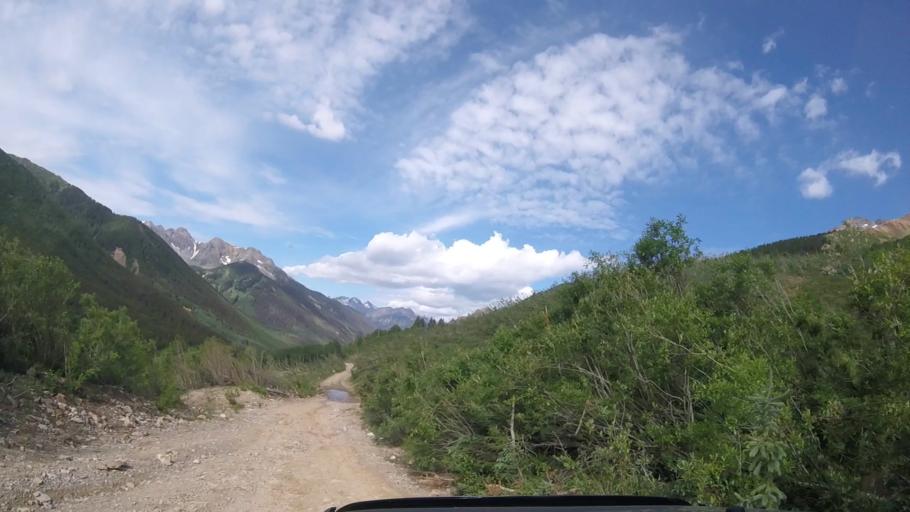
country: US
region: Colorado
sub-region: San Miguel County
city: Telluride
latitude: 37.8596
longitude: -107.8011
